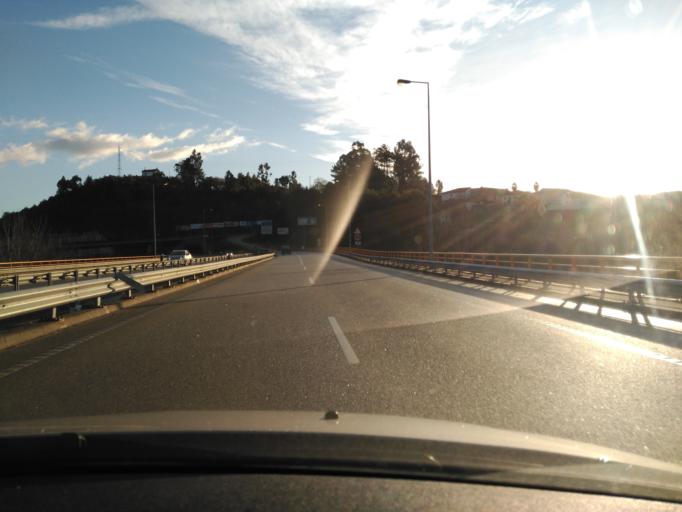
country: PT
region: Braga
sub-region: Fafe
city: Aroes
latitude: 41.4553
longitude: -8.1917
